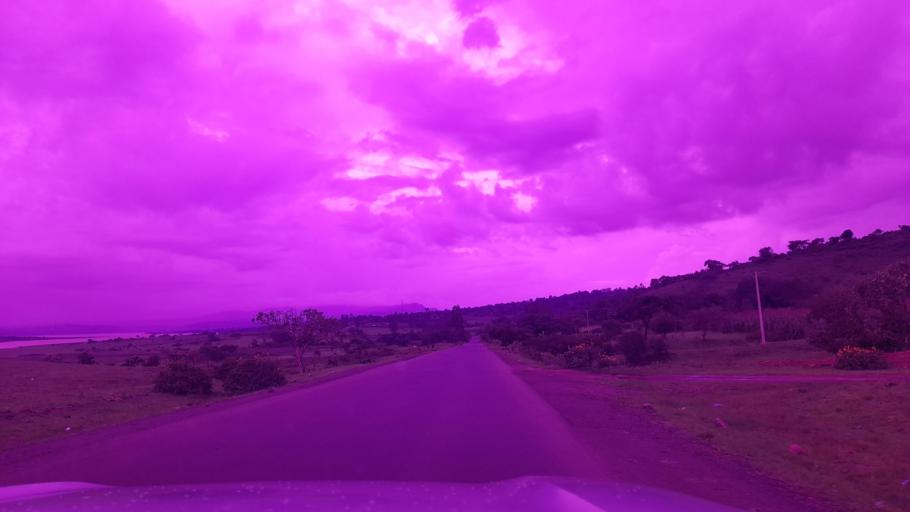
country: ET
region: Oromiya
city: Jima
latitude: 7.7763
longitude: 37.3417
